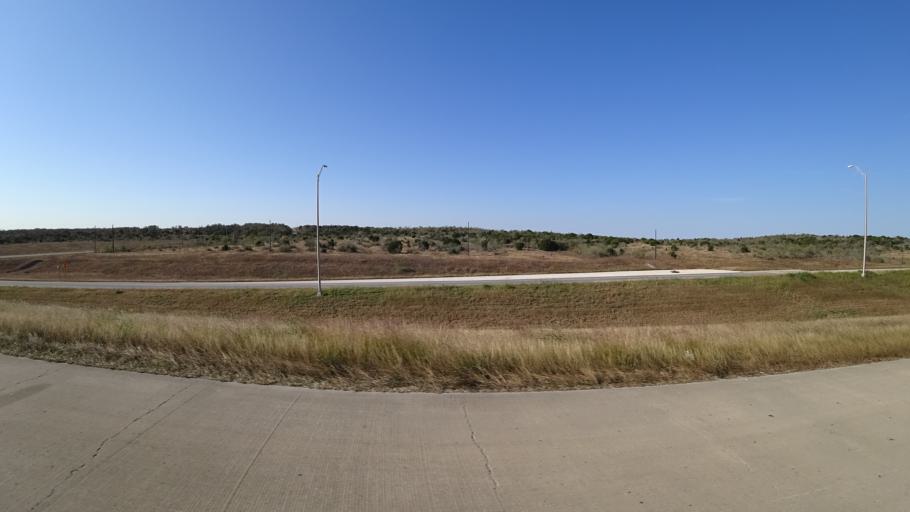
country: US
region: Texas
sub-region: Travis County
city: Manor
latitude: 30.3247
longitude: -97.5816
